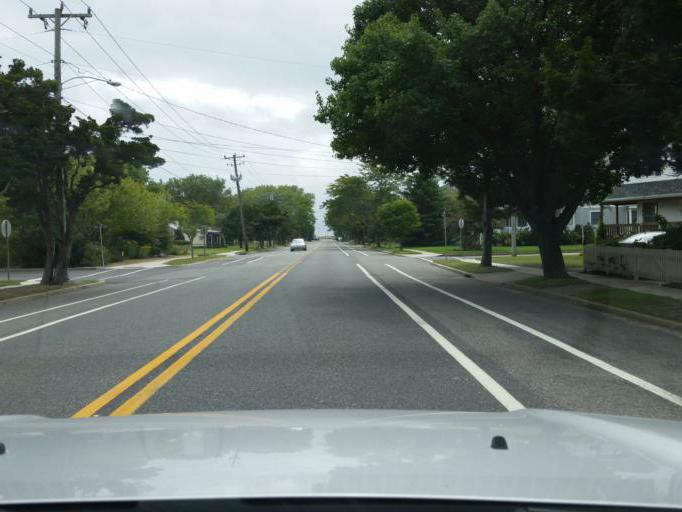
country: US
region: New Jersey
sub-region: Cape May County
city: Cape May
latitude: 38.9362
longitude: -74.9141
